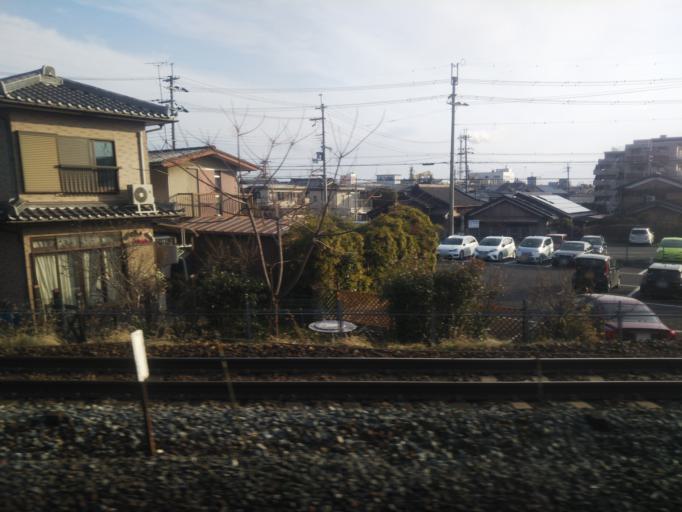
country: JP
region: Shiga Prefecture
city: Otsu-shi
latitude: 34.9828
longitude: 135.8938
